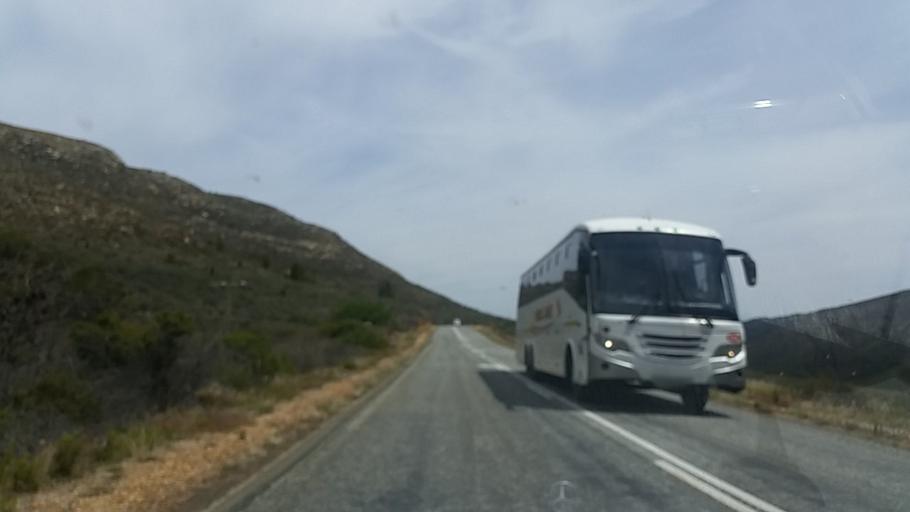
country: ZA
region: Western Cape
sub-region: Eden District Municipality
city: Knysna
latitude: -33.7454
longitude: 22.9888
